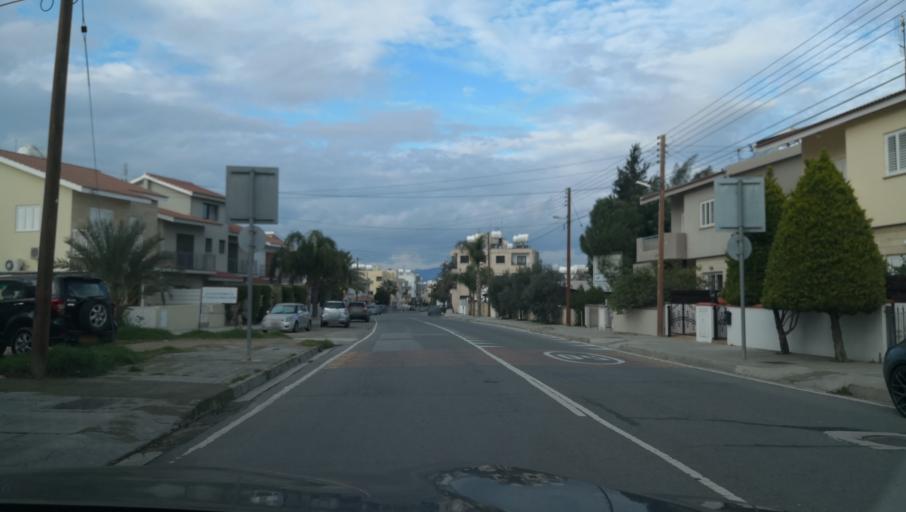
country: CY
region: Lefkosia
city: Nicosia
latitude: 35.1314
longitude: 33.3500
